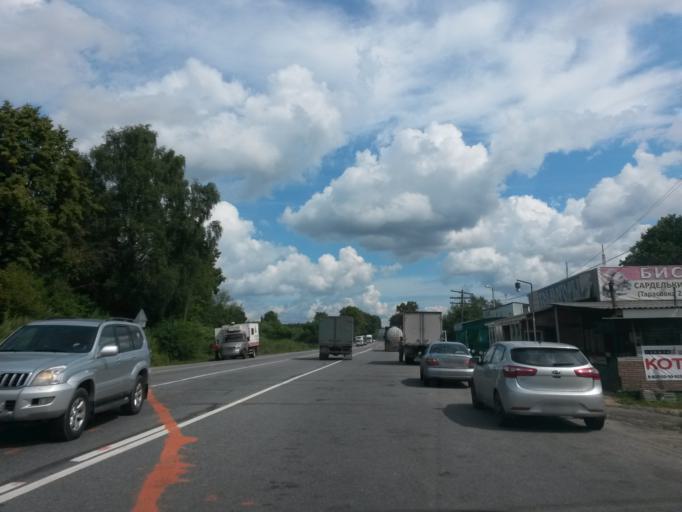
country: RU
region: Jaroslavl
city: Pereslavl'-Zalesskiy
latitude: 56.6570
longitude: 38.7032
